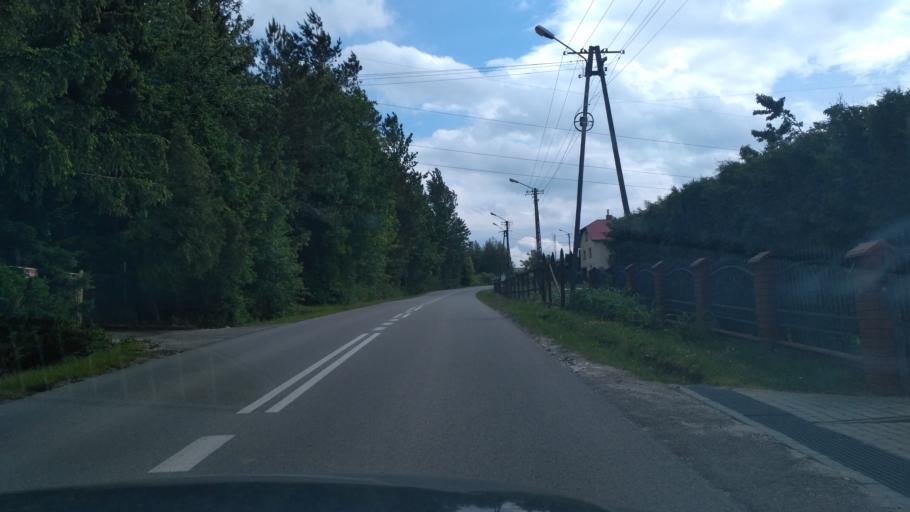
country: PL
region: Subcarpathian Voivodeship
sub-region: Powiat ropczycko-sedziszowski
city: Ropczyce
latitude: 50.0384
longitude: 21.6196
